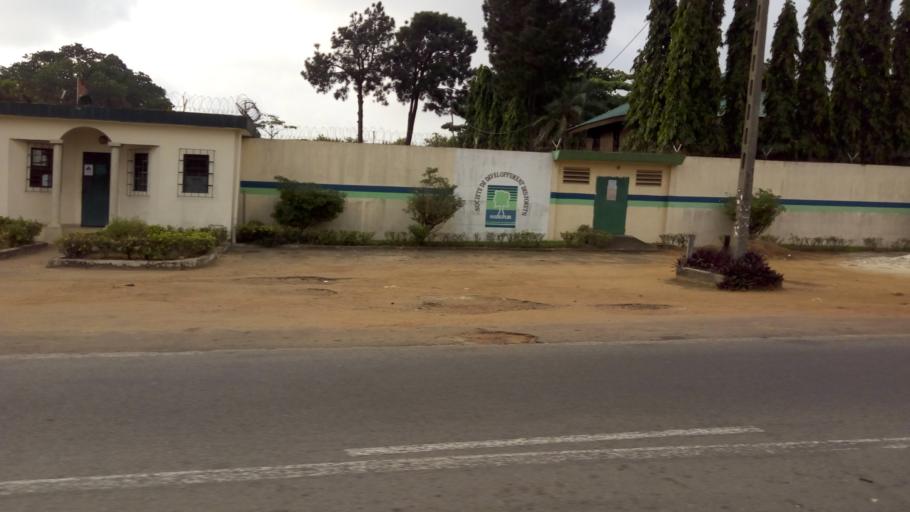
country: CI
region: Lagunes
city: Abidjan
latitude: 5.3487
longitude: -3.9984
